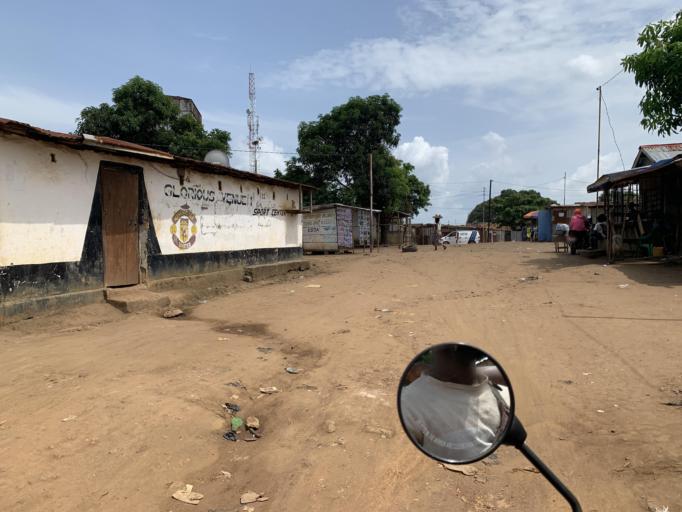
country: SL
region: Western Area
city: Hastings
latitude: 8.4083
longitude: -13.1337
